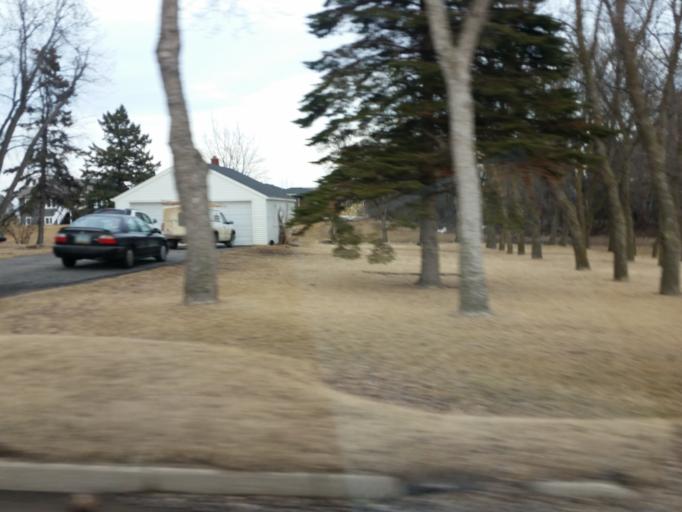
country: US
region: North Dakota
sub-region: Cass County
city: Casselton
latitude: 47.0991
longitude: -97.2180
